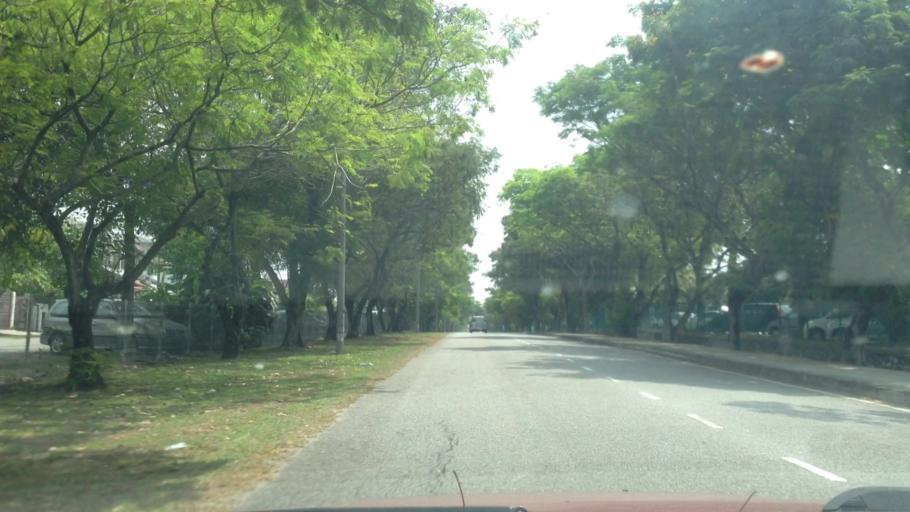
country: MY
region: Selangor
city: Subang Jaya
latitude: 3.0498
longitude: 101.5739
